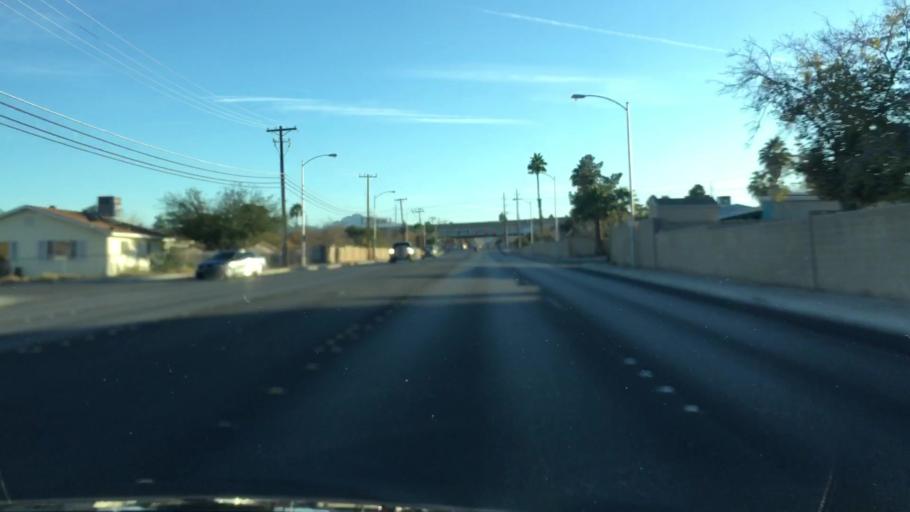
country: US
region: Nevada
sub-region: Clark County
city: Whitney
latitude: 36.0959
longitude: -115.0732
